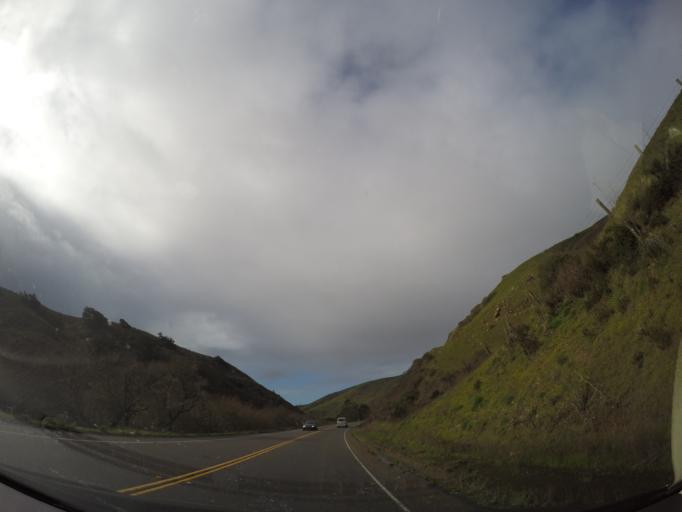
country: US
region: California
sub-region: Sonoma County
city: Bodega Bay
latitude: 38.3268
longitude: -123.0026
